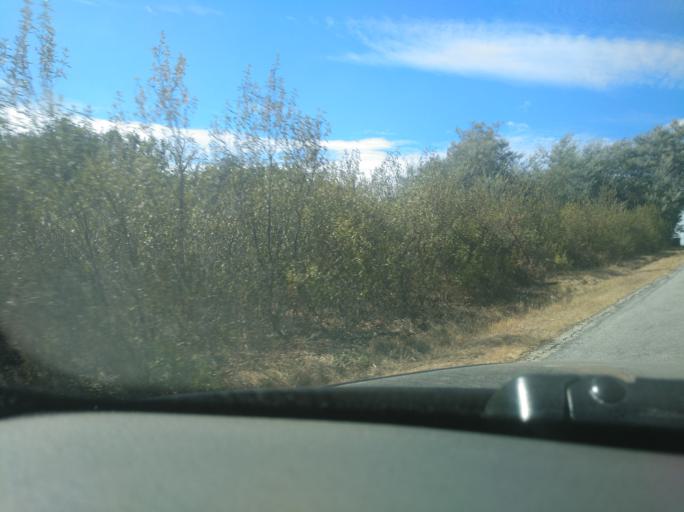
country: ES
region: Extremadura
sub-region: Provincia de Badajoz
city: La Codosera
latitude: 39.1470
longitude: -7.1572
